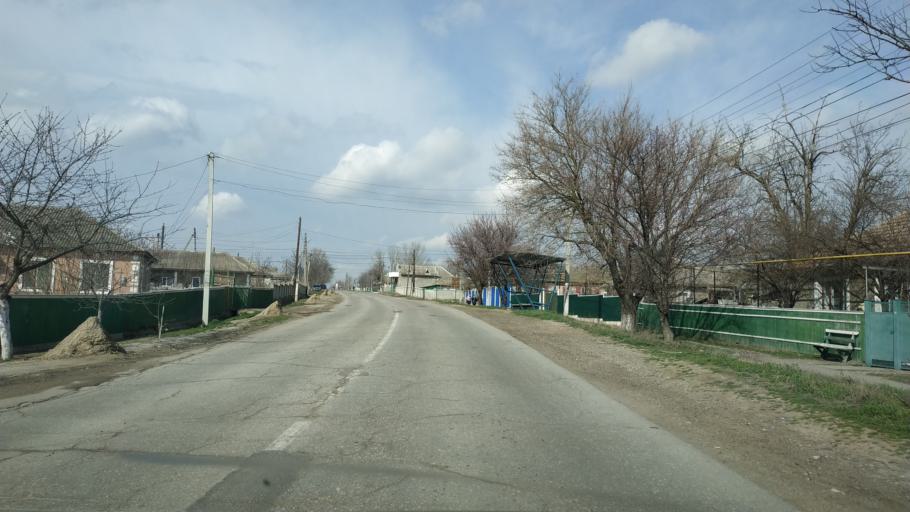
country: MD
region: Gagauzia
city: Vulcanesti
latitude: 45.6929
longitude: 28.4049
